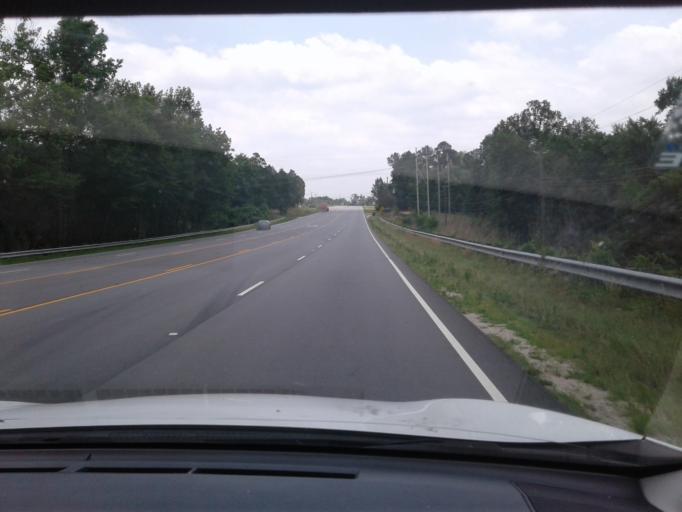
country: US
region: North Carolina
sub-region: Harnett County
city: Buies Creek
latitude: 35.3826
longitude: -78.7190
